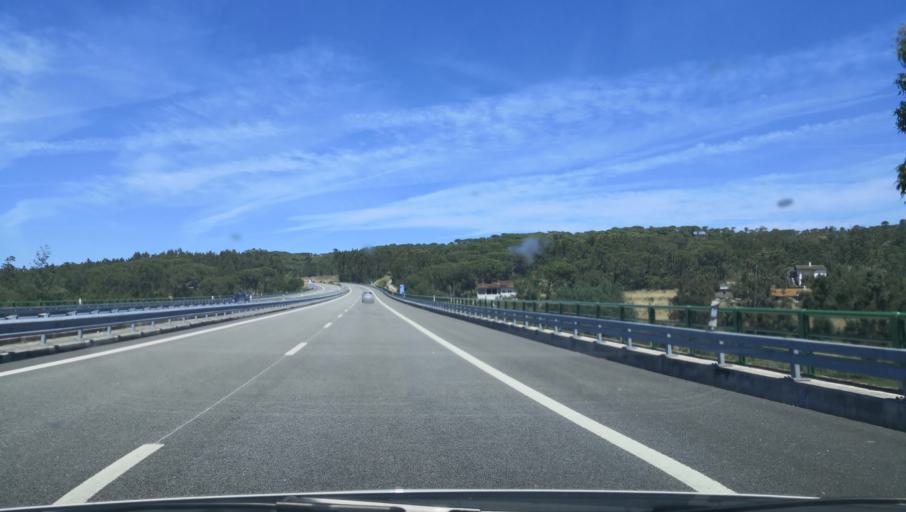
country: PT
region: Coimbra
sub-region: Montemor-O-Velho
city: Montemor-o-Velho
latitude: 40.1942
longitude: -8.6879
